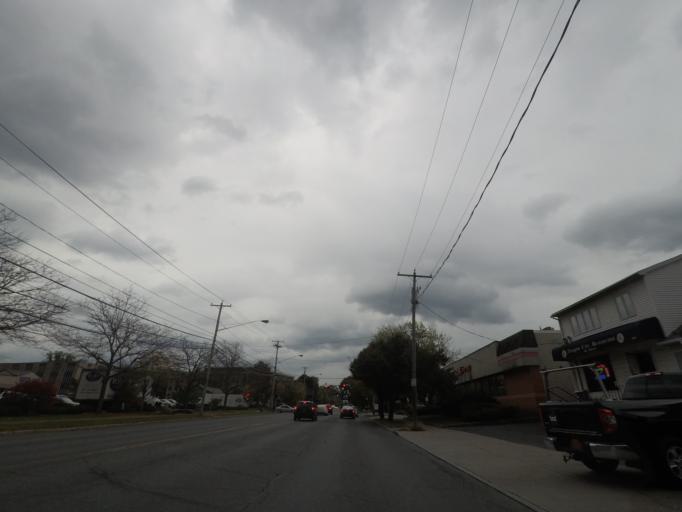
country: US
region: New York
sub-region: Albany County
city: McKownville
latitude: 42.6767
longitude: -73.8240
